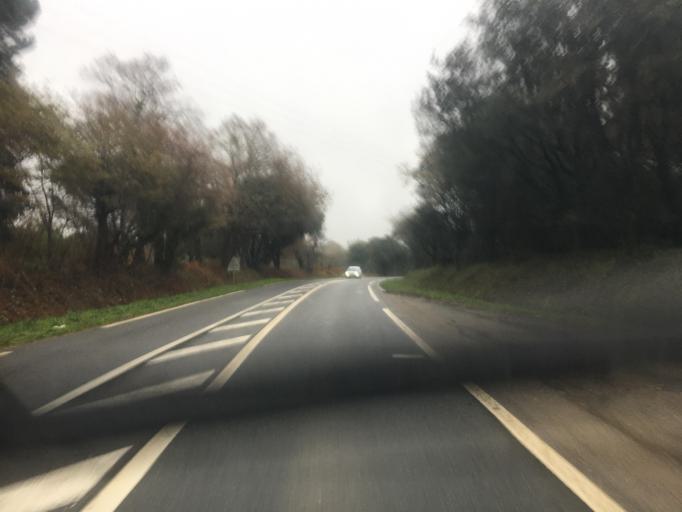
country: FR
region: Pays de la Loire
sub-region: Departement de la Loire-Atlantique
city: La Turballe
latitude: 47.3431
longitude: -2.4789
